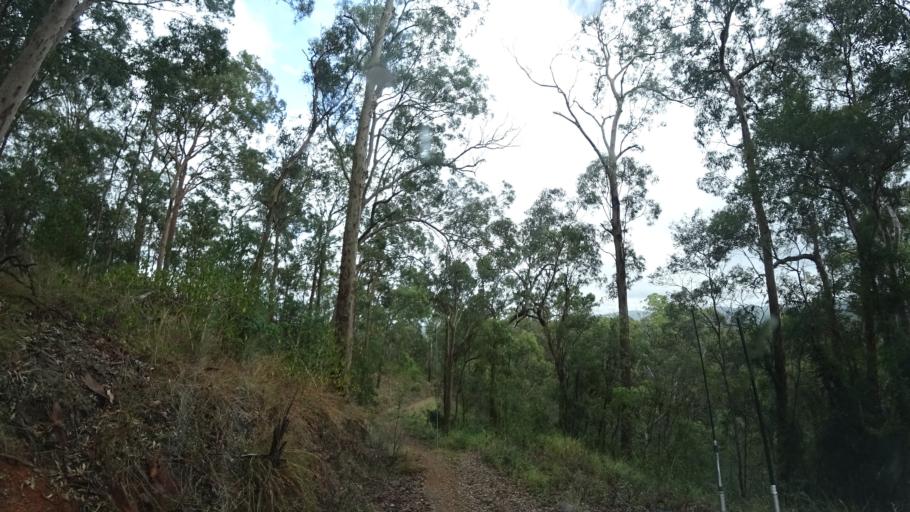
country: AU
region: Queensland
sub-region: Moreton Bay
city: Highvale
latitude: -27.4564
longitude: 152.8243
